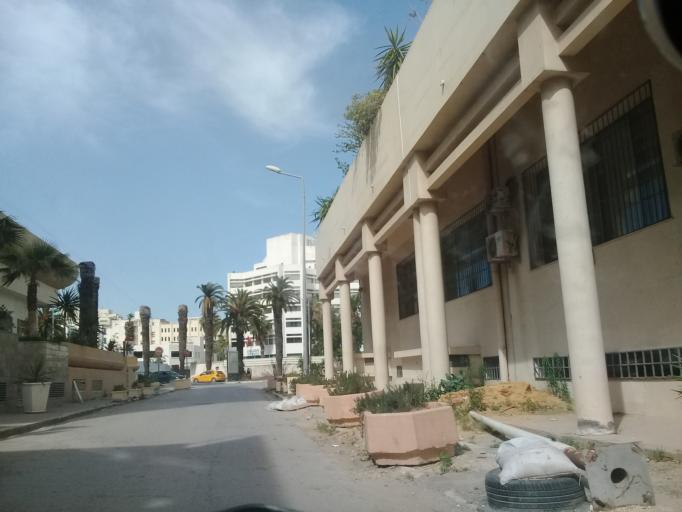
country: TN
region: Tunis
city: Tunis
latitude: 36.8163
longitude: 10.1830
